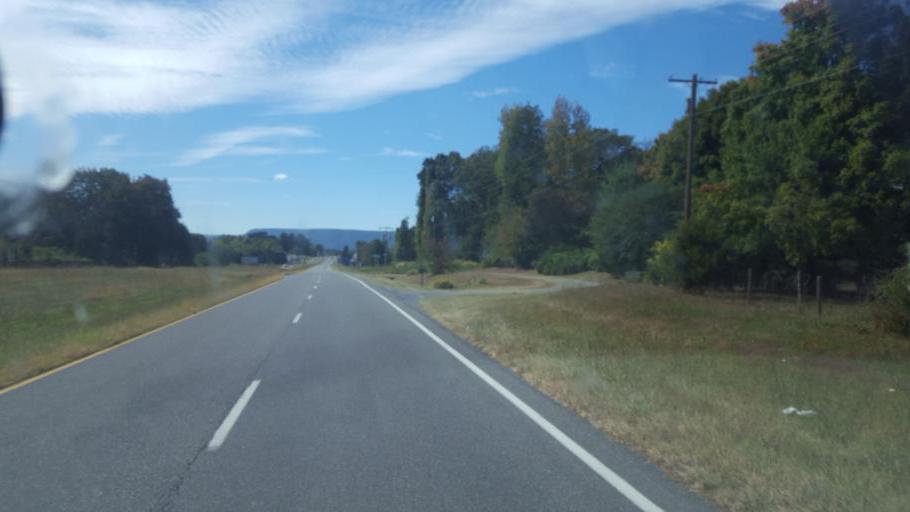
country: US
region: Virginia
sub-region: Page County
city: Luray
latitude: 38.6742
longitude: -78.3975
